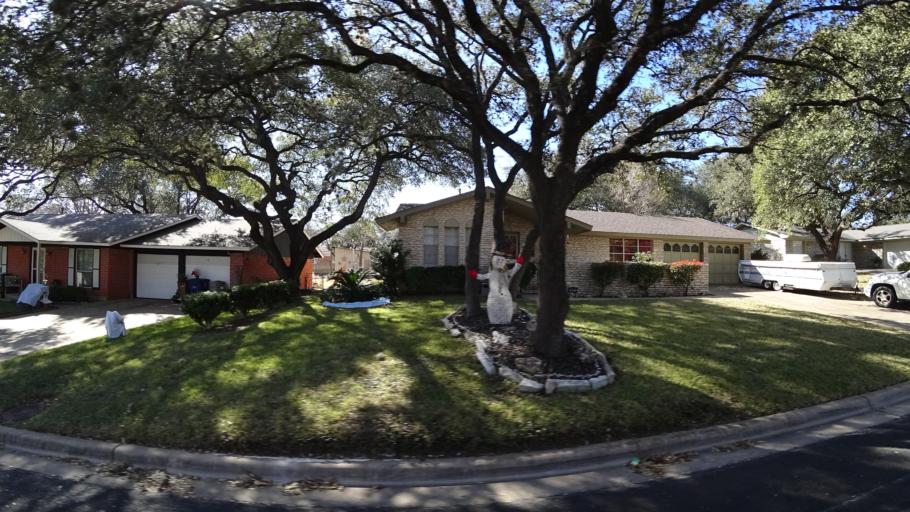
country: US
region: Texas
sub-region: Travis County
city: Wells Branch
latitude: 30.3881
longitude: -97.6879
